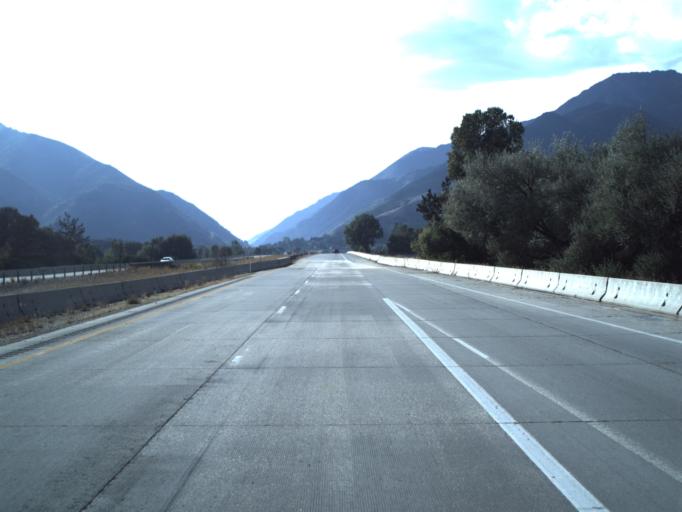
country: US
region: Utah
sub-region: Morgan County
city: Mountain Green
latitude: 41.1380
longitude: -111.8021
